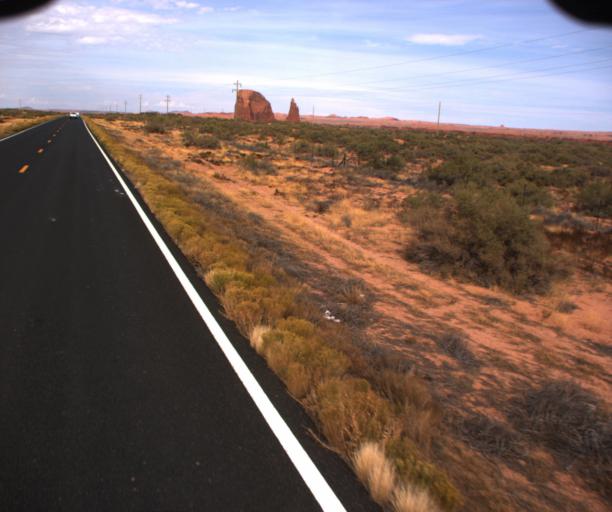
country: US
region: Arizona
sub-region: Apache County
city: Many Farms
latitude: 36.6363
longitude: -109.5870
